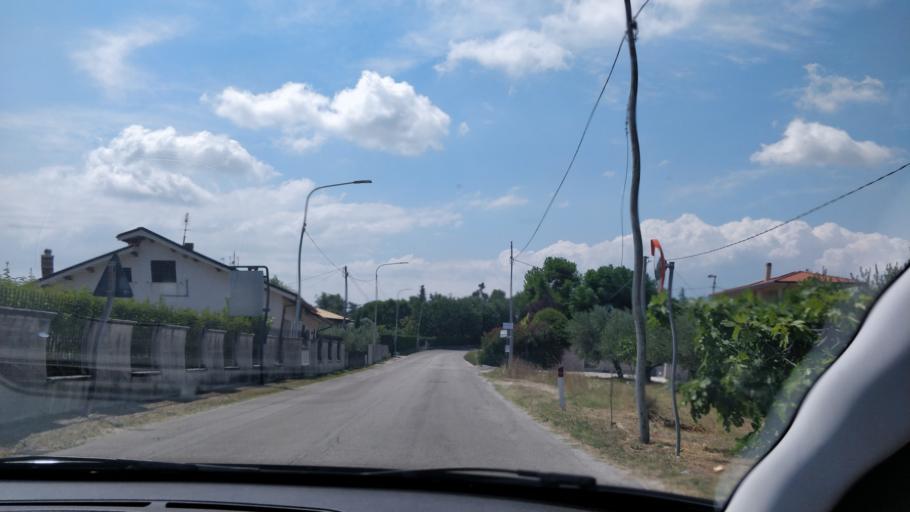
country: IT
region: Abruzzo
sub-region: Provincia di Chieti
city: Torrevecchia
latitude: 42.3992
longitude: 14.2125
